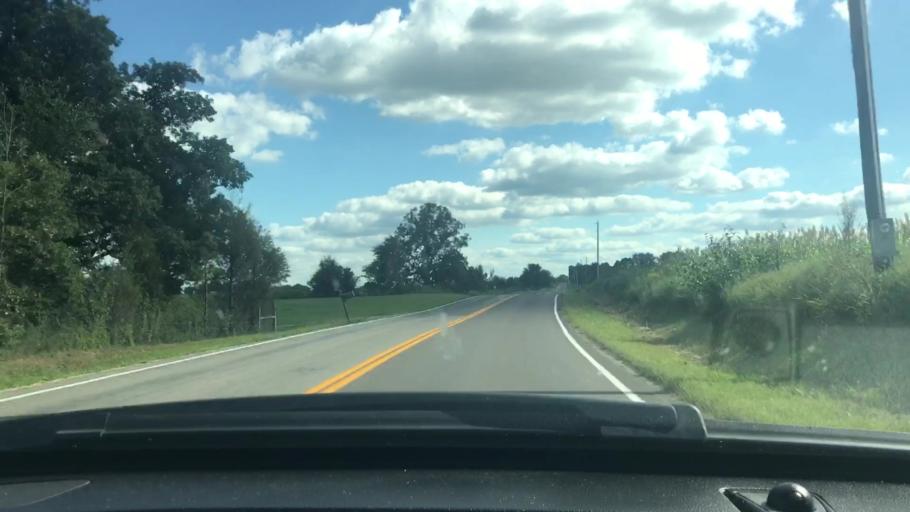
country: US
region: Missouri
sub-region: Wright County
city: Mountain Grove
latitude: 37.1755
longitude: -92.2670
